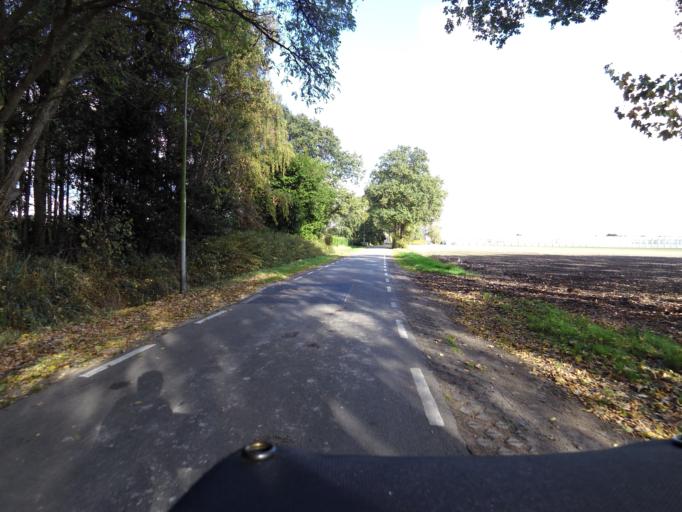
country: NL
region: North Brabant
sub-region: Gemeente Bergen op Zoom
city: Lepelstraat
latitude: 51.5521
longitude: 4.2770
